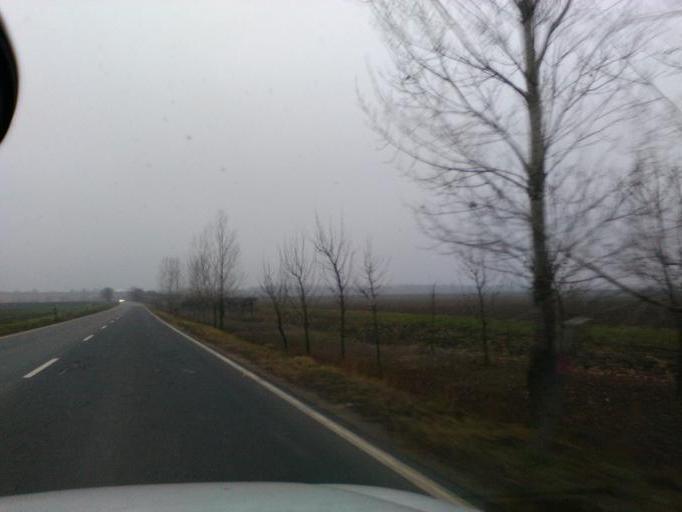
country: HU
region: Pest
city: Tarnok
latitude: 47.3805
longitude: 18.8244
